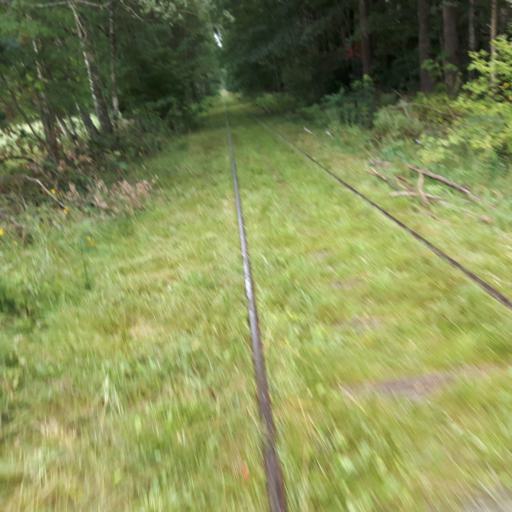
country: SE
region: Skane
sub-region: Ostra Goinge Kommun
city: Broby
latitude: 56.2632
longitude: 14.0715
